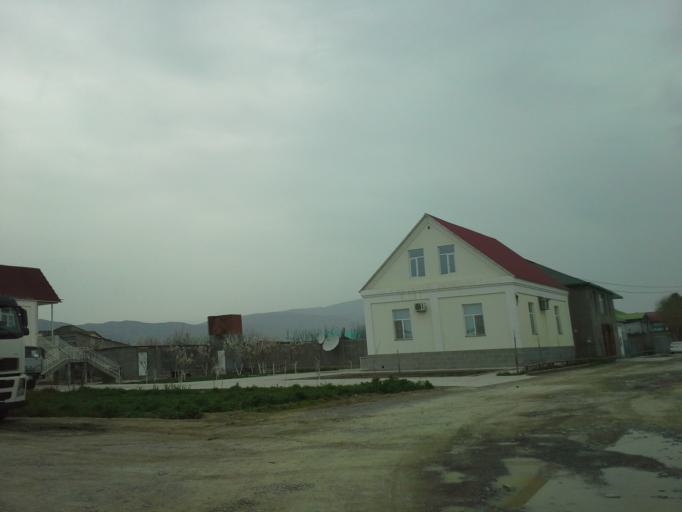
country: TM
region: Ahal
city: Abadan
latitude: 37.9712
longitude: 58.2297
